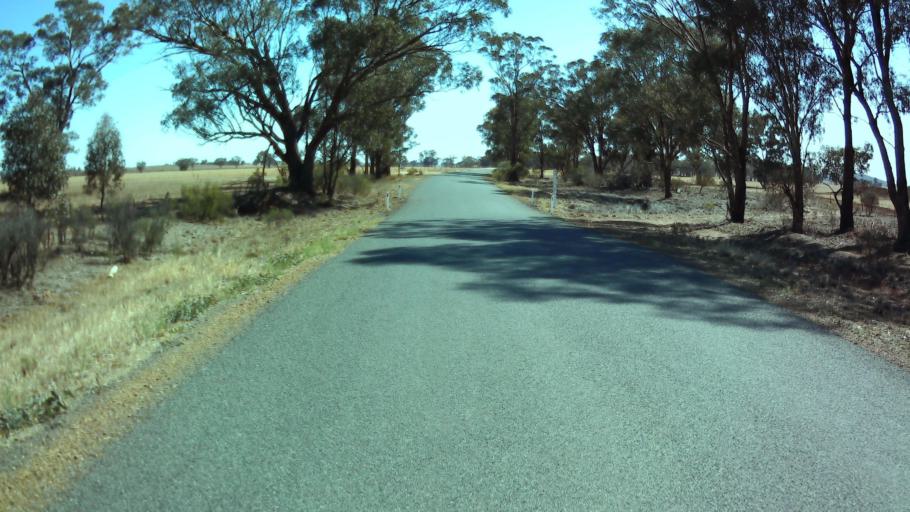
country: AU
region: New South Wales
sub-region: Weddin
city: Grenfell
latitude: -33.7374
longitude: 147.8835
